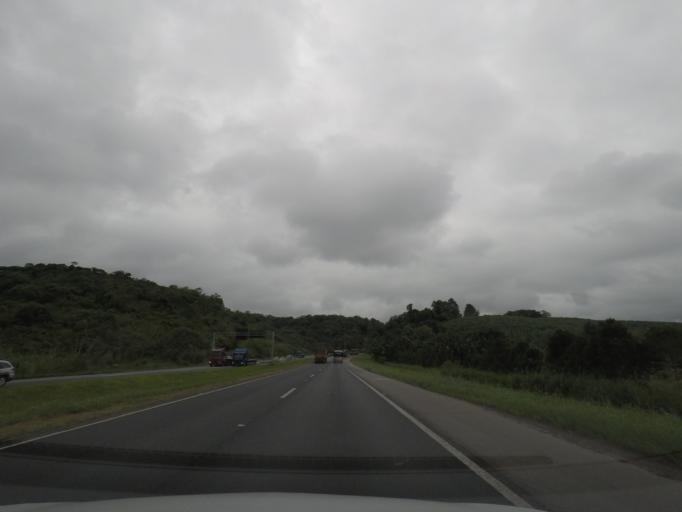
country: BR
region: Sao Paulo
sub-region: Juquia
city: Juquia
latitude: -24.3971
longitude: -47.7294
